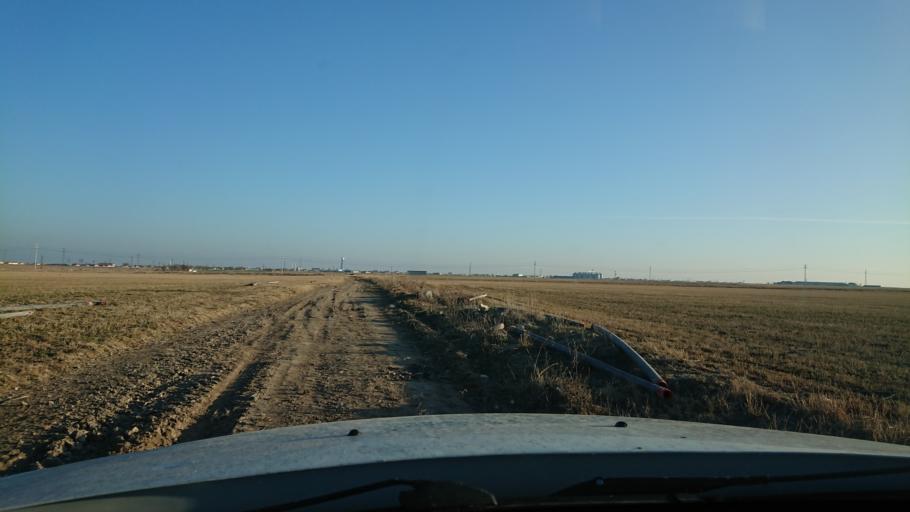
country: TR
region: Aksaray
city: Sultanhani
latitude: 38.2680
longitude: 33.5198
